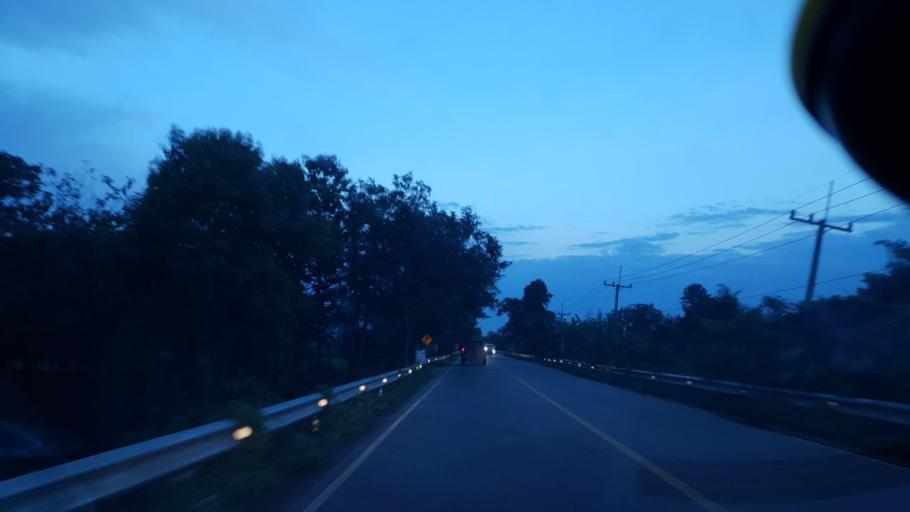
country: TH
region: Chiang Rai
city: Wiang Chiang Rung
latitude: 19.9708
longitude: 99.9795
